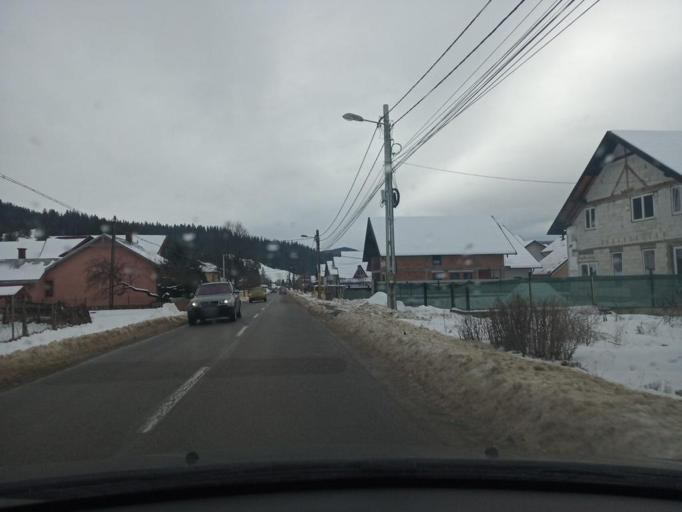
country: RO
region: Suceava
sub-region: Comuna Manastirea Humorului
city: Manastirea Humorului
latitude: 47.5732
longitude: 25.8792
